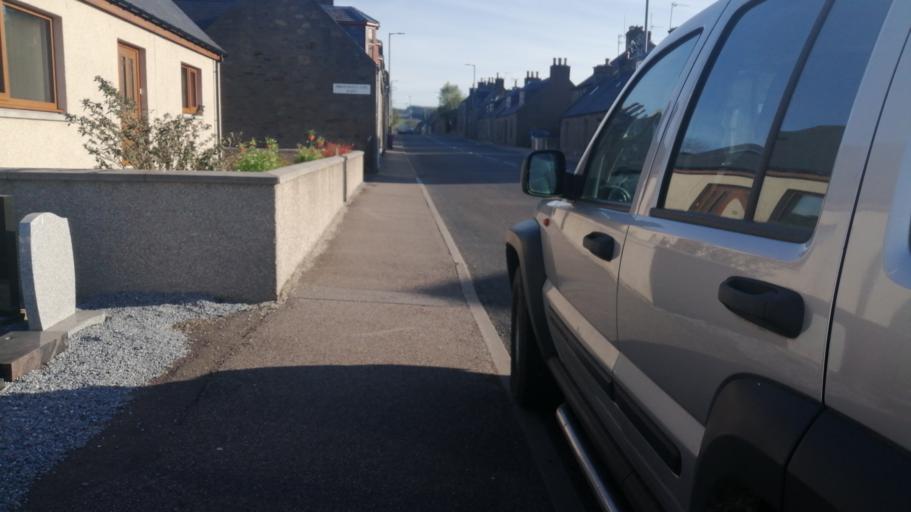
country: GB
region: Scotland
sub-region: Moray
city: Keith
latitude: 57.5410
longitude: -2.9482
